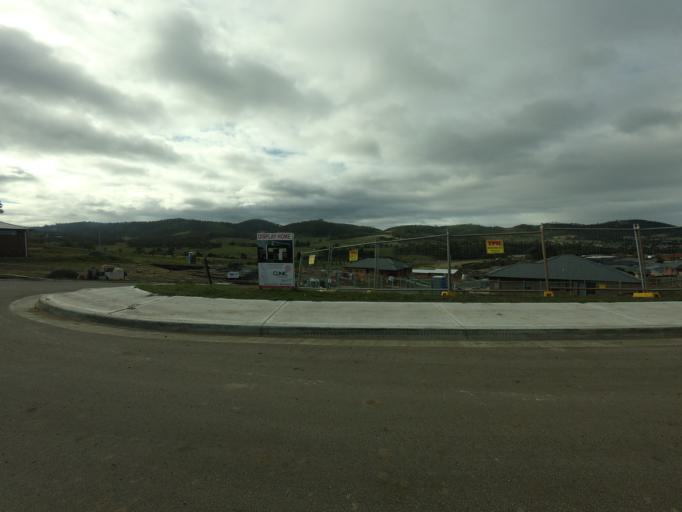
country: AU
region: Tasmania
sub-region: Clarence
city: Howrah
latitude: -42.8823
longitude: 147.4215
